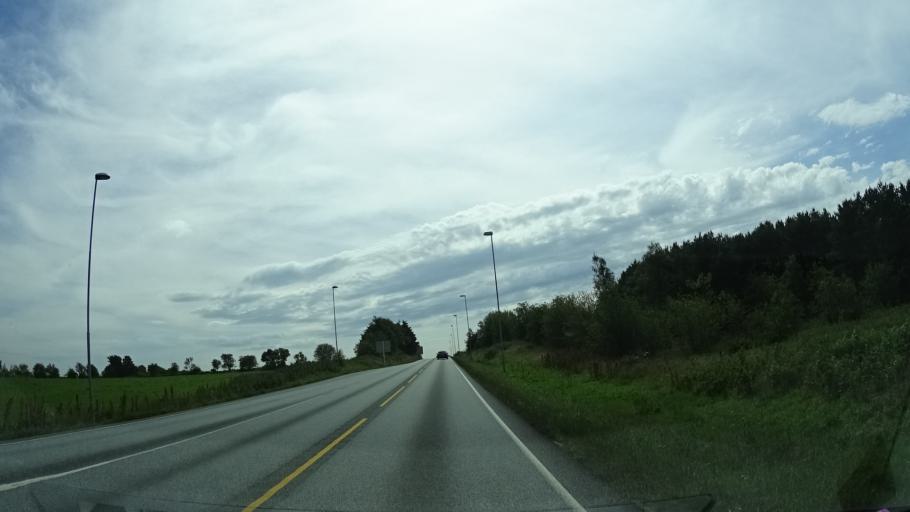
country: NO
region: Rogaland
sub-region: Randaberg
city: Randaberg
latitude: 59.0048
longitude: 5.6427
